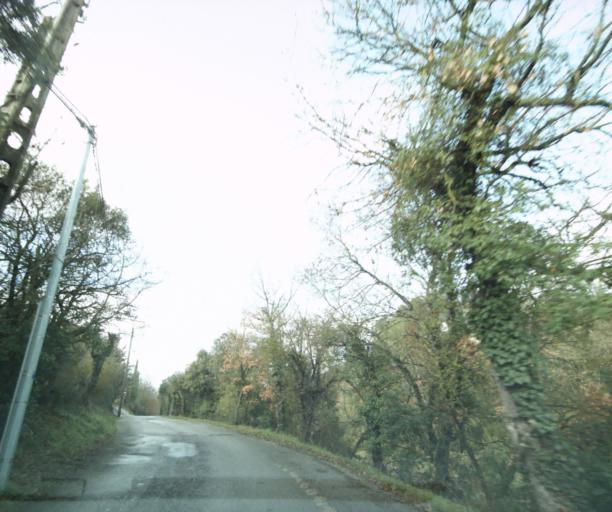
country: FR
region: Provence-Alpes-Cote d'Azur
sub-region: Departement du Var
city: Tourves
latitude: 43.4059
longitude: 5.9175
